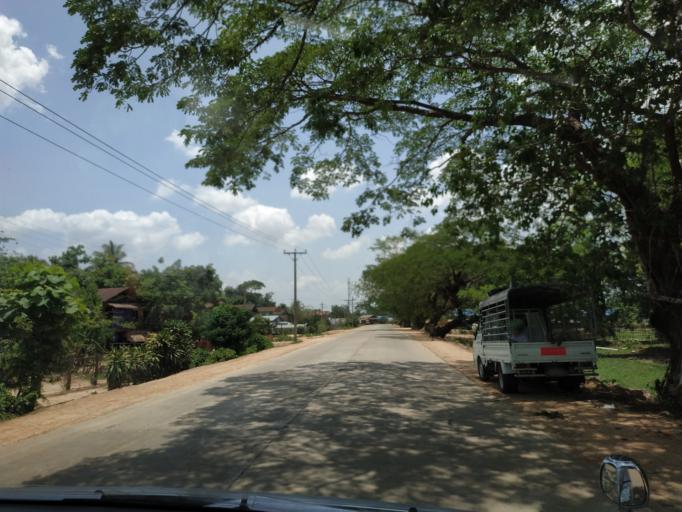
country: MM
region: Bago
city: Bago
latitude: 17.4790
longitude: 96.4850
